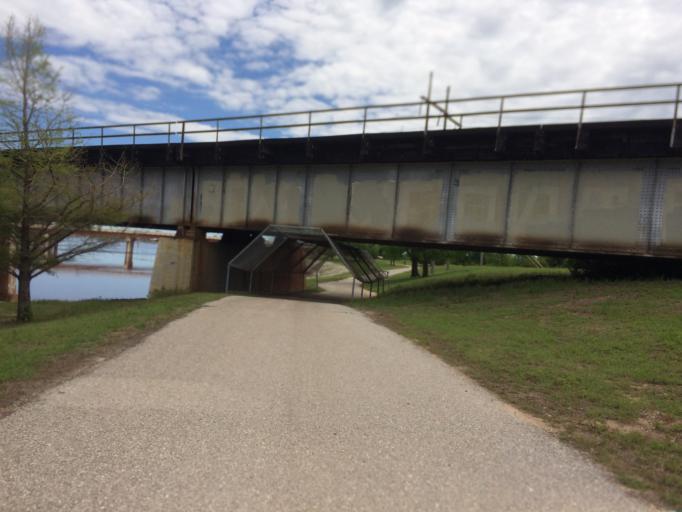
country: US
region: Oklahoma
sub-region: Oklahoma County
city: Oklahoma City
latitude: 35.4477
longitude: -97.5134
